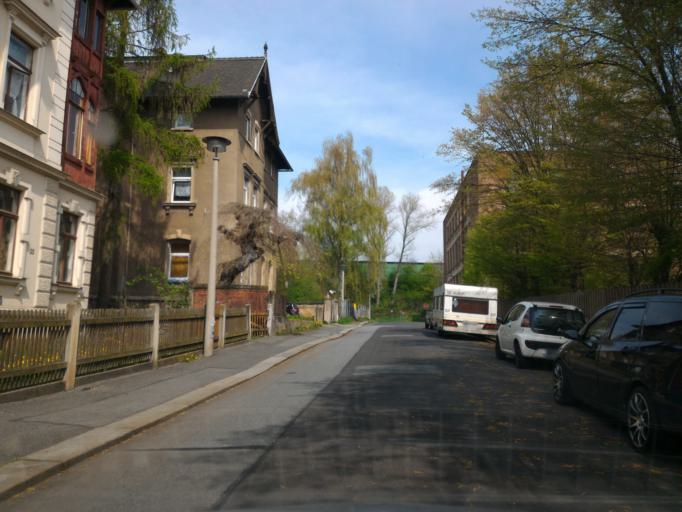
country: DE
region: Saxony
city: Zittau
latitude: 50.9025
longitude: 14.8030
